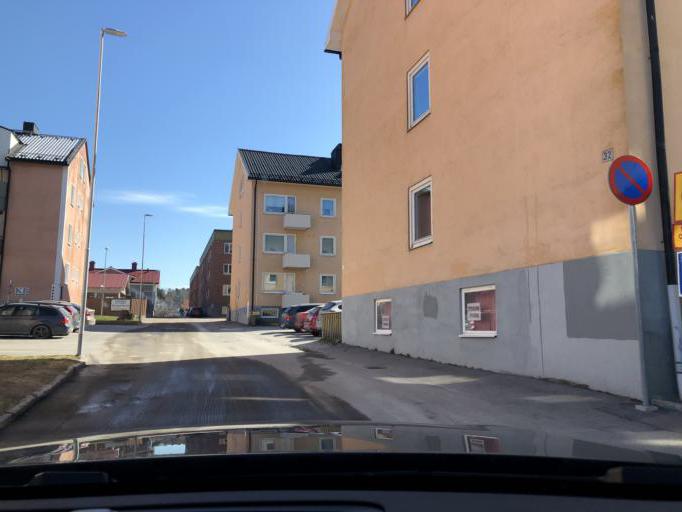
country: SE
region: Gaevleborg
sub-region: Hudiksvalls Kommun
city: Hudiksvall
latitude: 61.7293
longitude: 17.1141
